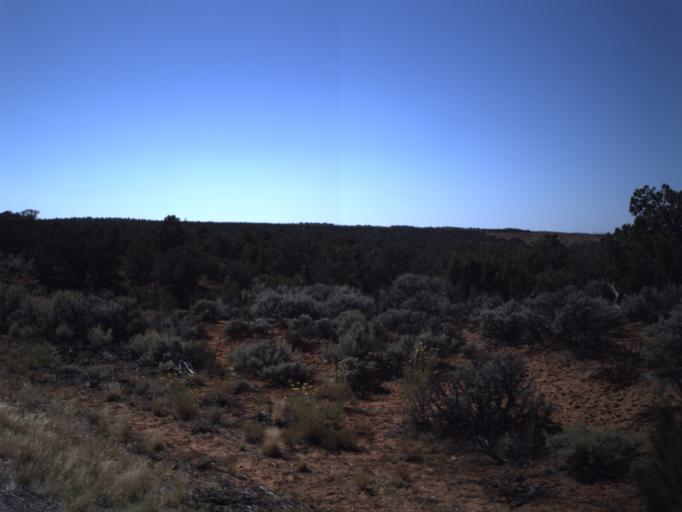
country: US
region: Utah
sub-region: San Juan County
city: Blanding
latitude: 37.3193
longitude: -109.9190
